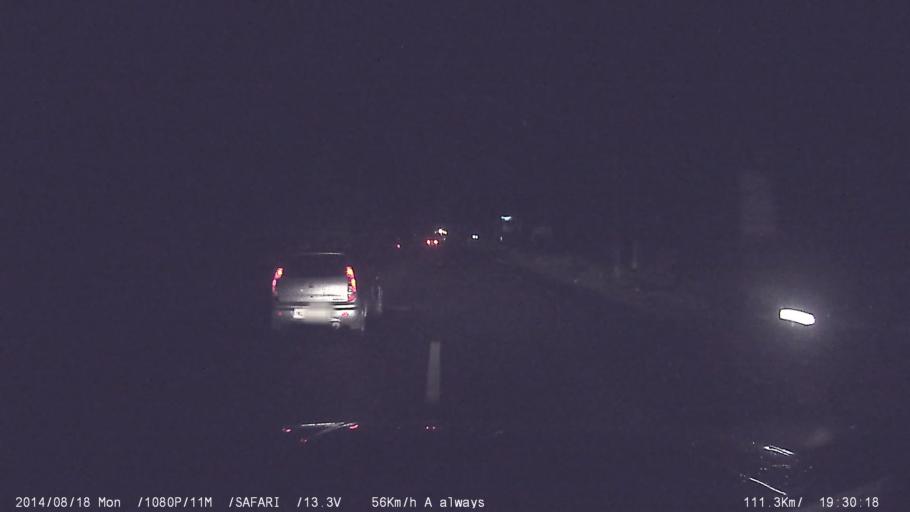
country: IN
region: Kerala
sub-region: Ernakulam
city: Perumbavoor
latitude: 10.0875
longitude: 76.5000
